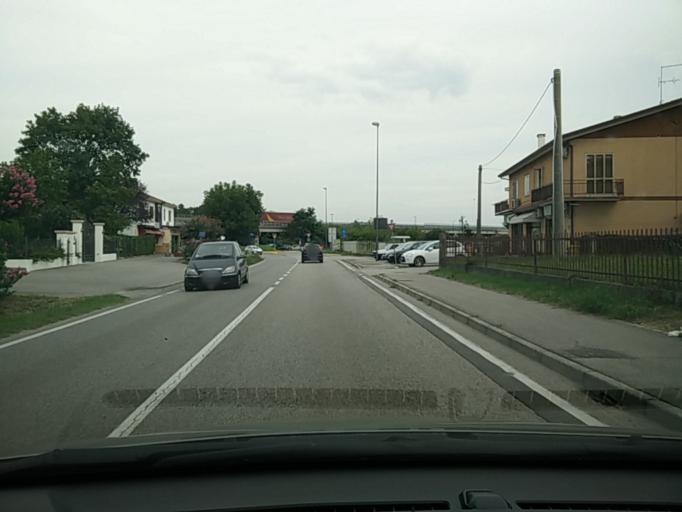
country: IT
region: Veneto
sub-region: Provincia di Treviso
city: Castagnole
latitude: 45.6677
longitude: 12.1910
